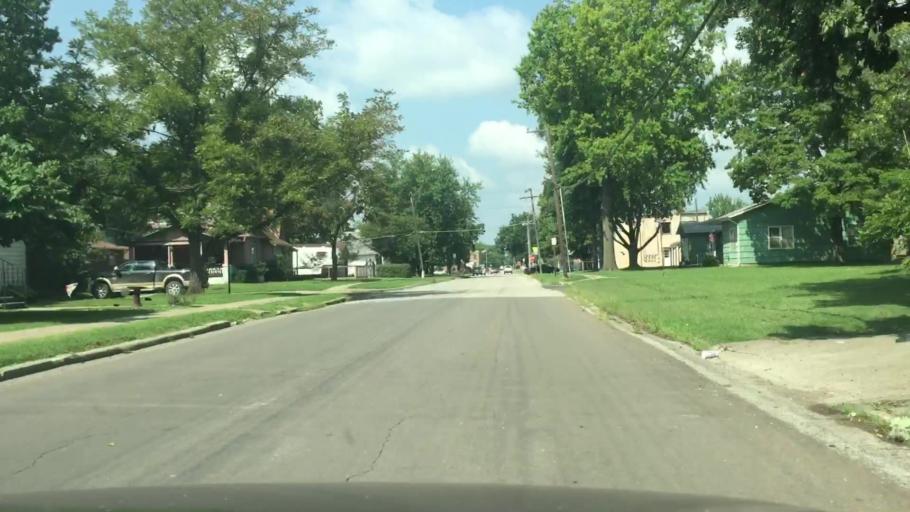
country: US
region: Kansas
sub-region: Allen County
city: Iola
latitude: 37.9200
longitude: -95.4006
